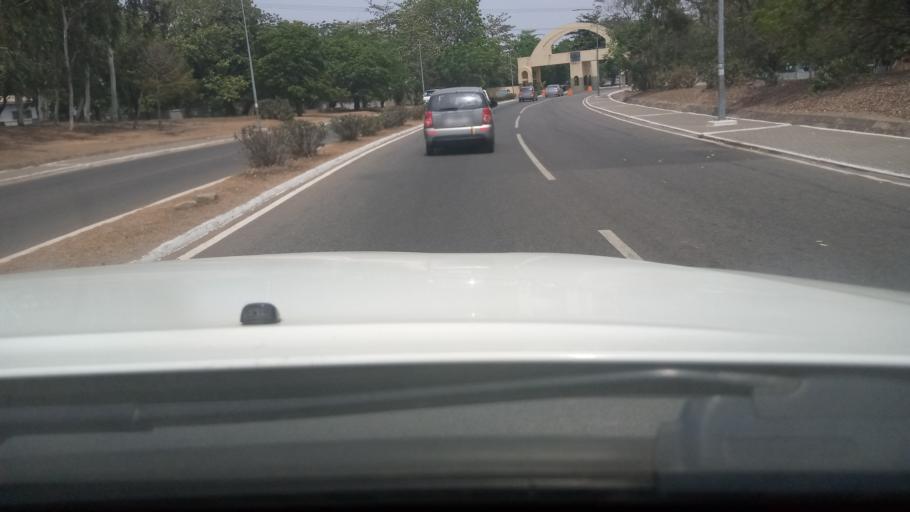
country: GH
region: Greater Accra
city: Accra
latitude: 5.5882
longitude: -0.1619
